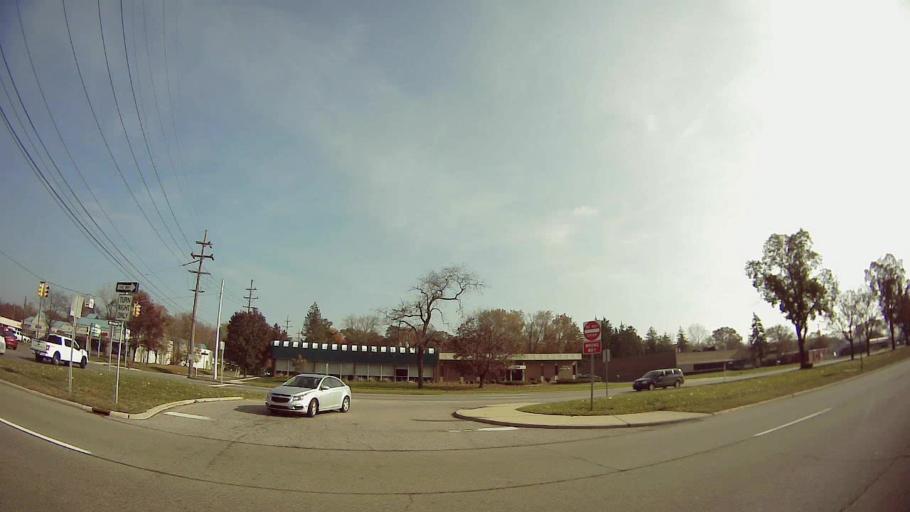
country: US
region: Michigan
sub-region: Oakland County
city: Southfield
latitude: 42.4557
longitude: -83.2787
